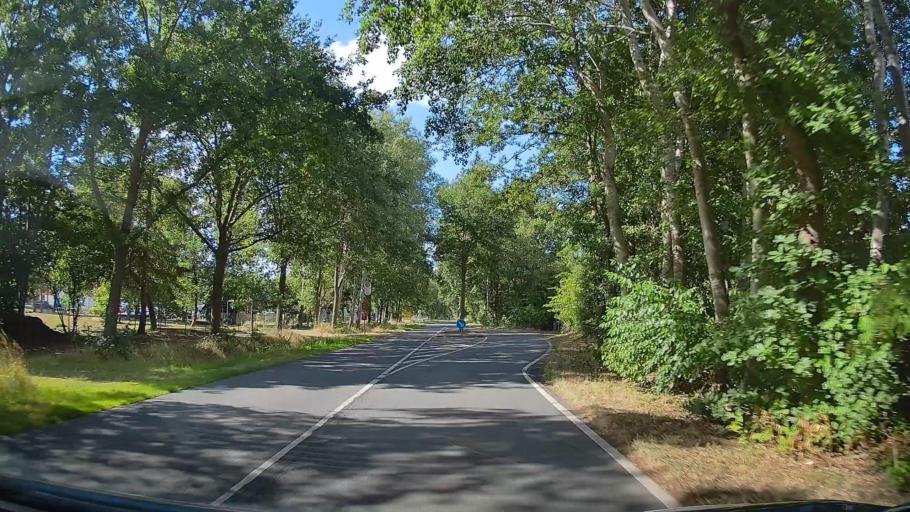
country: DE
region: Lower Saxony
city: Rieste
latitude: 52.4905
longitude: 7.9913
